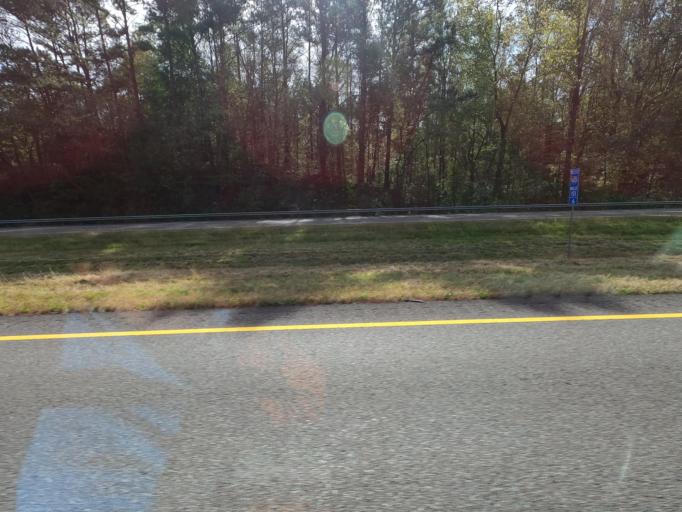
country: US
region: Tennessee
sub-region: Hickman County
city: Centerville
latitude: 35.8893
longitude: -87.6541
